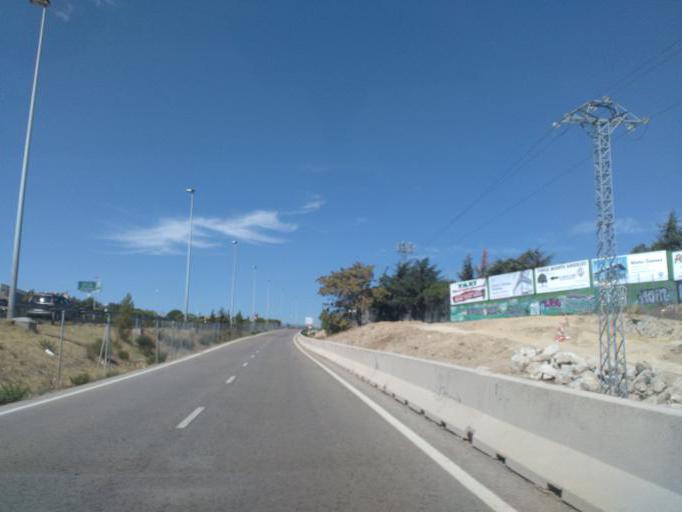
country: ES
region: Madrid
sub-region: Provincia de Madrid
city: Torrelodones
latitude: 40.5709
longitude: -3.9212
